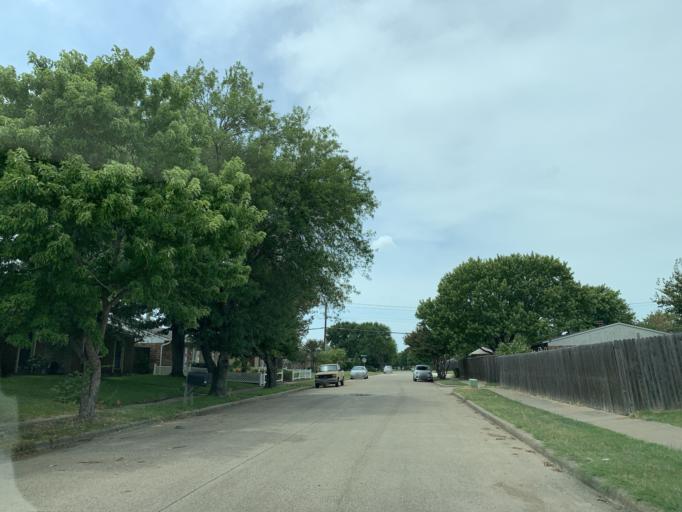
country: US
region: Texas
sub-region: Dallas County
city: Cedar Hill
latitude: 32.6534
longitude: -97.0270
